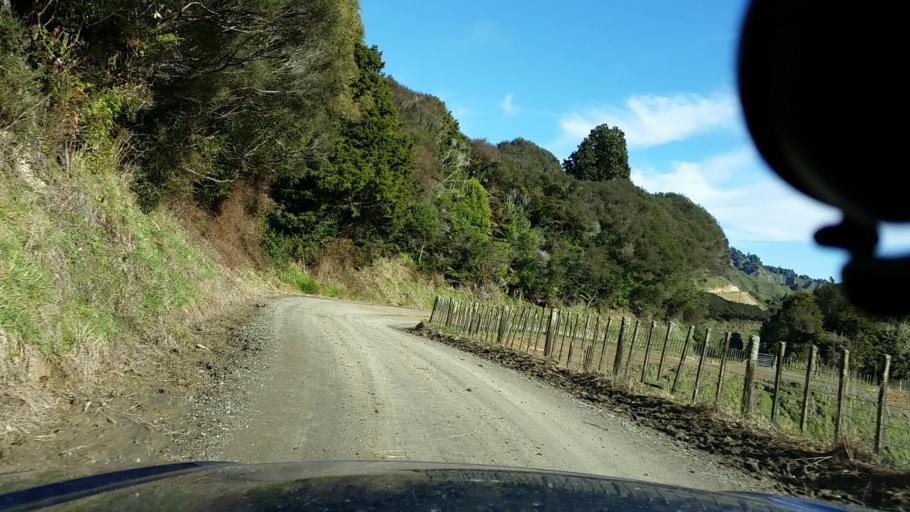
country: NZ
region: Taranaki
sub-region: New Plymouth District
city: Waitara
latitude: -39.0501
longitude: 174.7643
